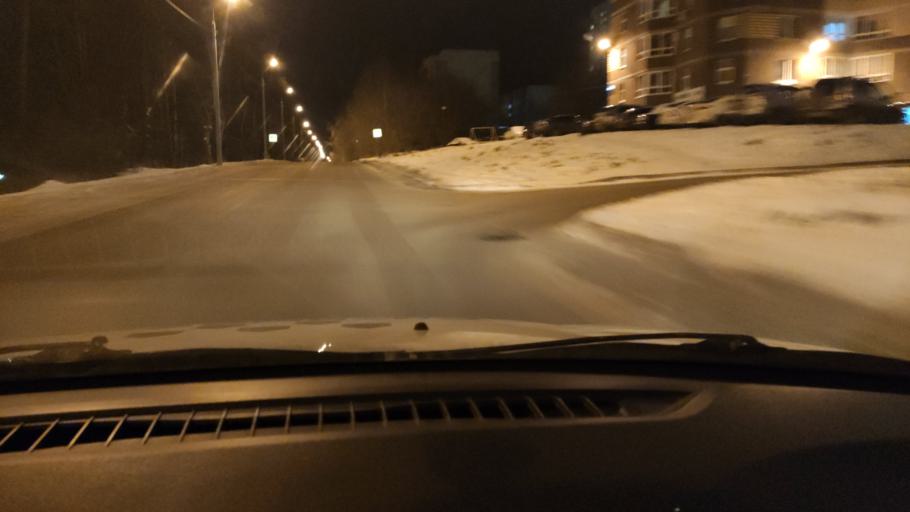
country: RU
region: Perm
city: Perm
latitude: 58.1014
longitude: 56.3072
